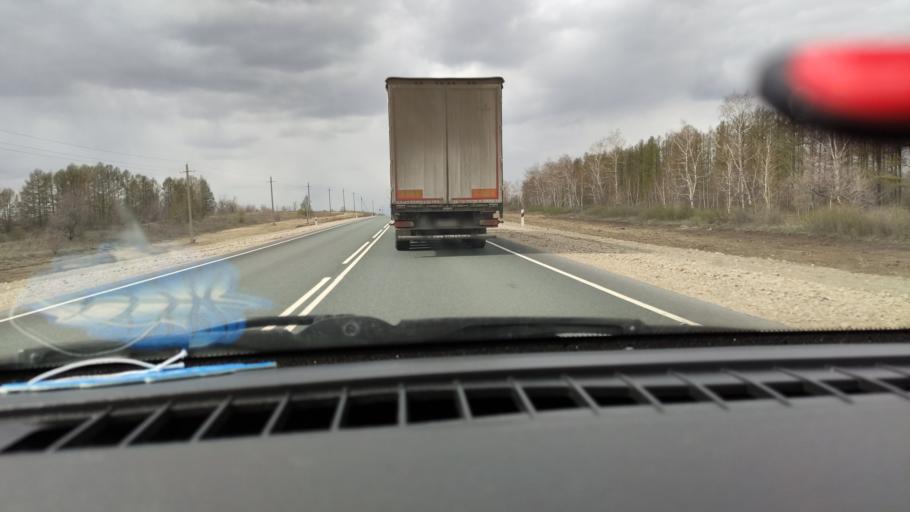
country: RU
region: Saratov
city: Shikhany
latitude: 52.1612
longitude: 47.1125
